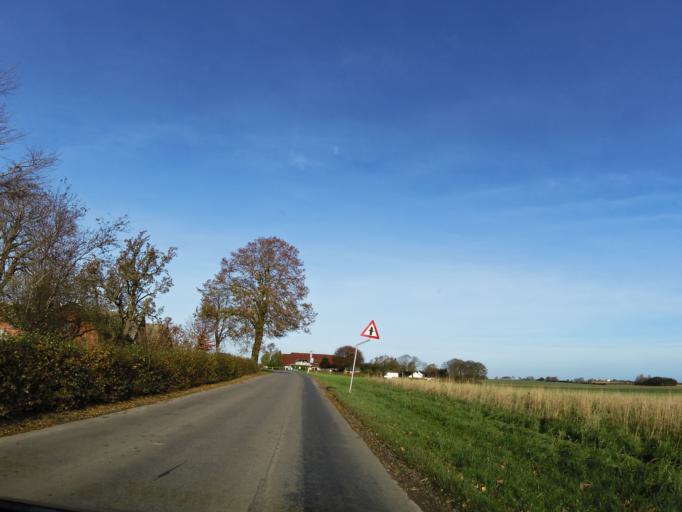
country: DK
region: Central Jutland
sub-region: Odder Kommune
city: Odder
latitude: 55.9383
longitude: 10.2357
